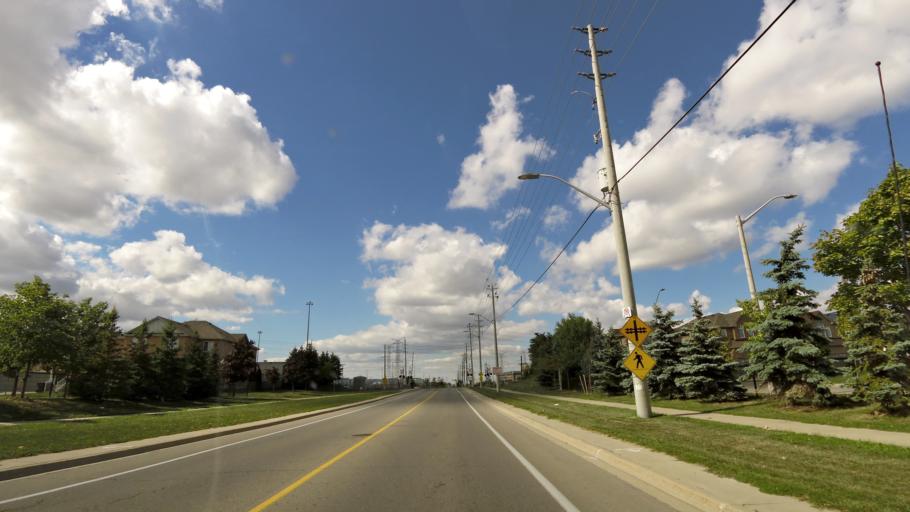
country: CA
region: Ontario
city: Brampton
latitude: 43.5910
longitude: -79.7861
